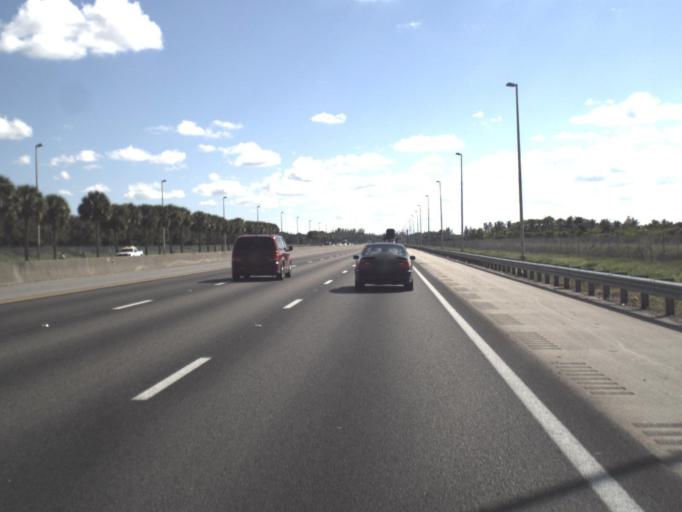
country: US
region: Florida
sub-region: Palm Beach County
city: Villages of Oriole
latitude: 26.4967
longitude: -80.1727
